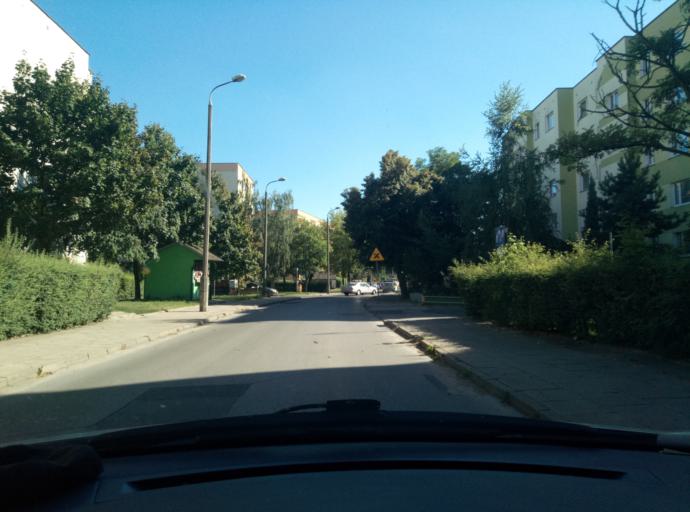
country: PL
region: Kujawsko-Pomorskie
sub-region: Torun
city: Torun
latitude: 53.0251
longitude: 18.5993
